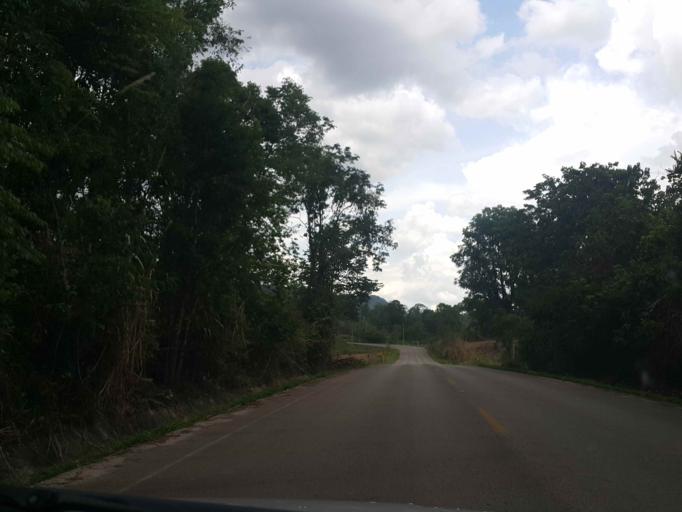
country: TH
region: Lampang
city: Ngao
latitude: 18.9360
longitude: 100.0831
